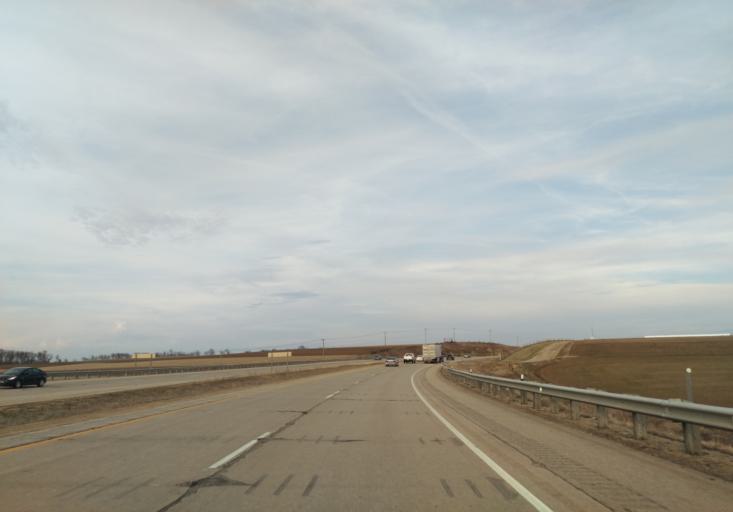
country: US
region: Wisconsin
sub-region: Iowa County
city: Barneveld
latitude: 43.0085
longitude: -89.9546
